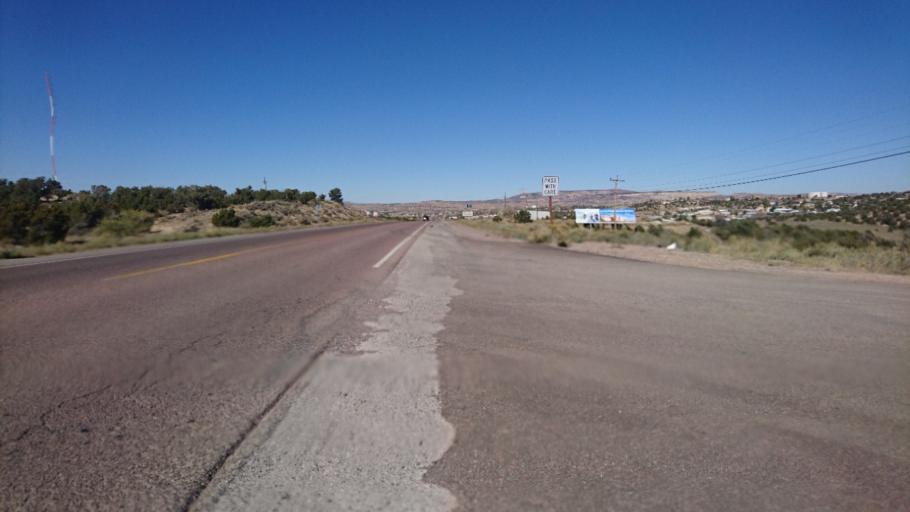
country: US
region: New Mexico
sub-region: McKinley County
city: Gallup
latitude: 35.4917
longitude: -108.7408
